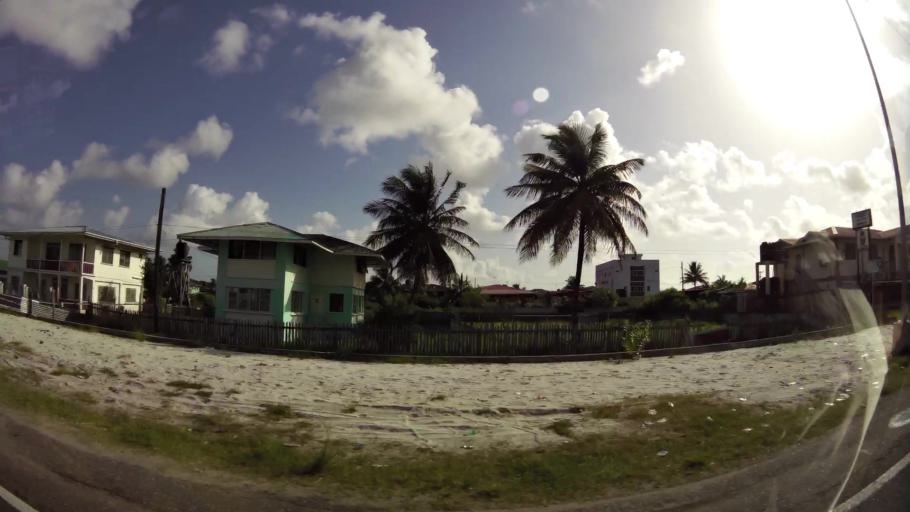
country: GY
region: Demerara-Mahaica
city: Georgetown
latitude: 6.8140
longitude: -58.0679
